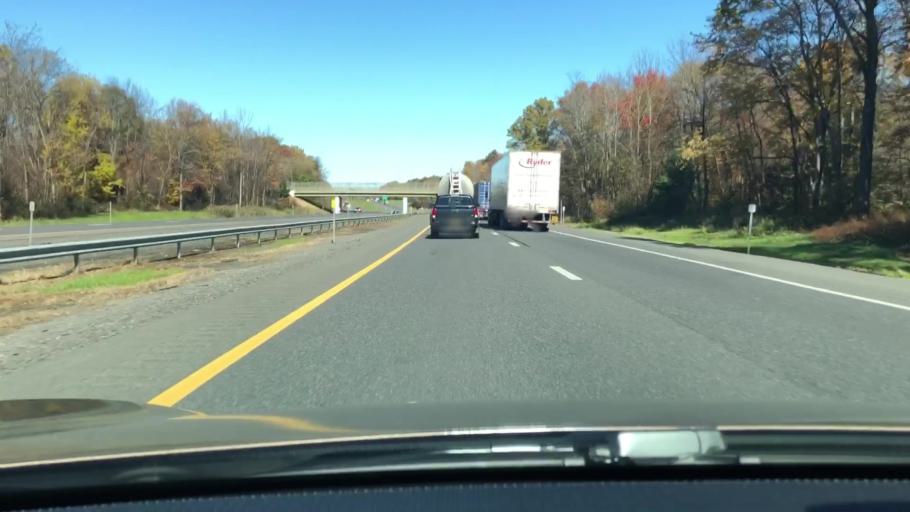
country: US
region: New York
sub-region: Ulster County
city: Clintondale
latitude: 41.7087
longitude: -74.0754
